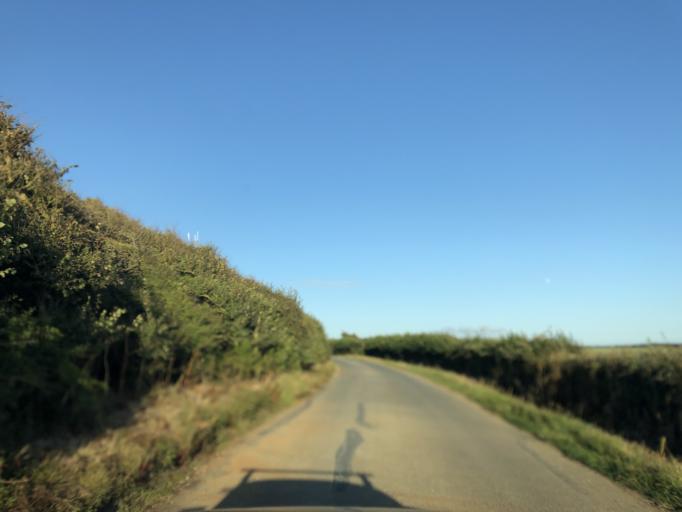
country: GB
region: England
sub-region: Isle of Wight
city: Shalfleet
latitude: 50.6335
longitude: -1.3878
